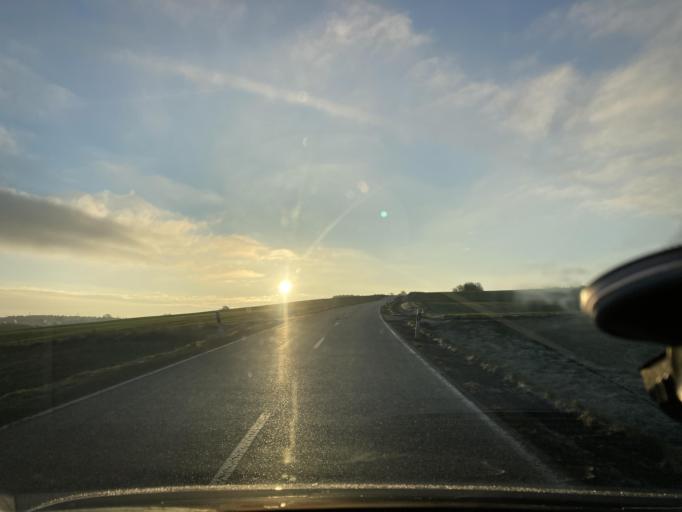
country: DE
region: Rheinland-Pfalz
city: Altlay
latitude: 49.9825
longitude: 7.2799
